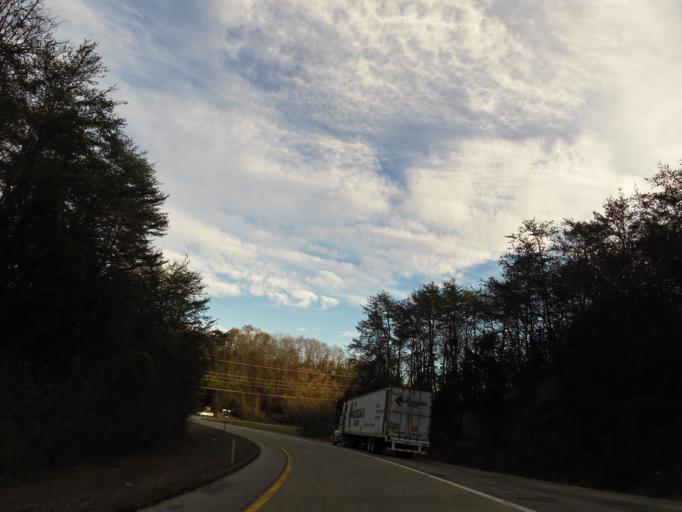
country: US
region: Tennessee
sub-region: Knox County
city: Mascot
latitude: 35.9953
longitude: -83.7010
